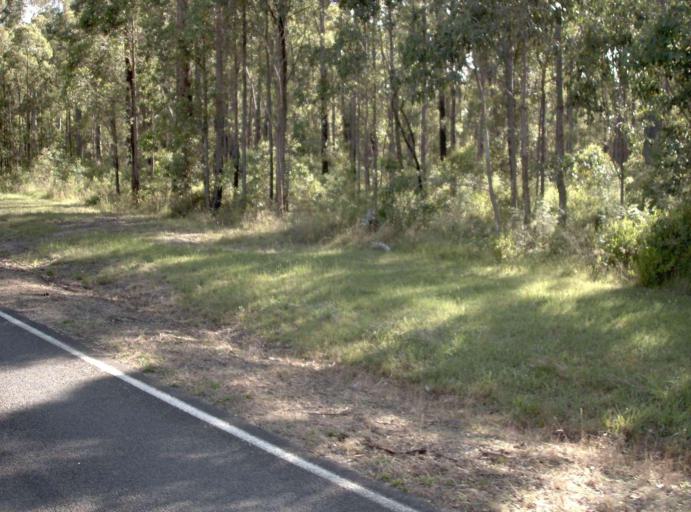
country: AU
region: Victoria
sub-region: East Gippsland
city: Lakes Entrance
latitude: -37.6842
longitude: 148.4699
